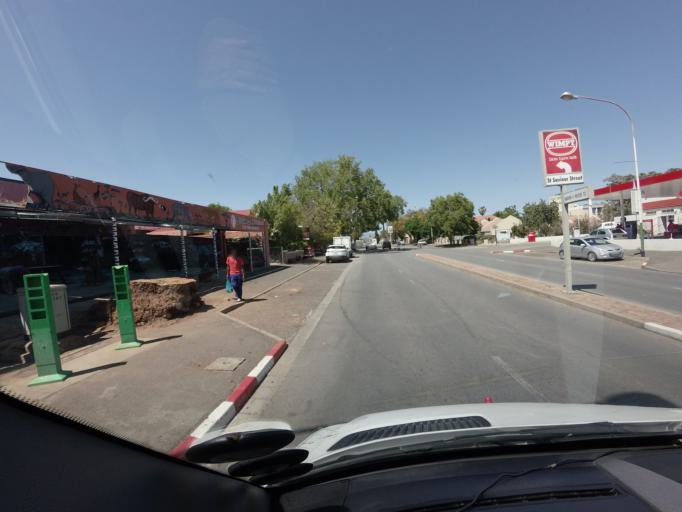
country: ZA
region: Western Cape
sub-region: Eden District Municipality
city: Oudtshoorn
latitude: -33.5864
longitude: 22.2038
